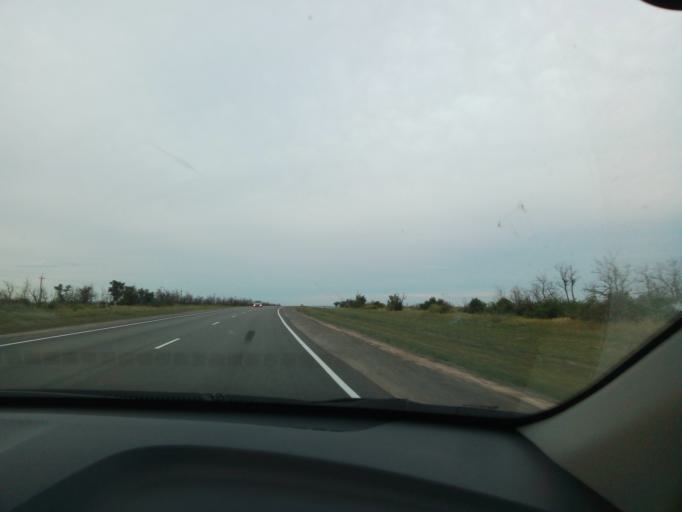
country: RU
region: Volgograd
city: Dubovka
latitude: 49.1544
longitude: 44.8420
